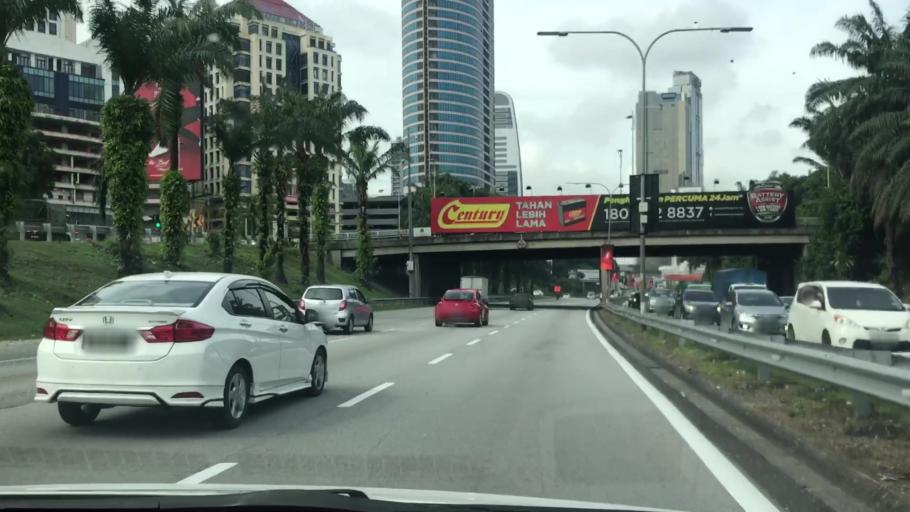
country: MY
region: Selangor
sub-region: Petaling
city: Petaling Jaya
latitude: 3.1069
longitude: 101.6477
